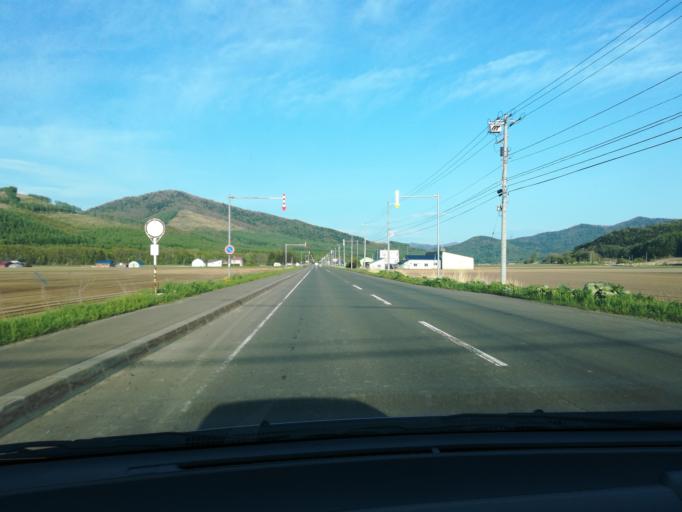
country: JP
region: Hokkaido
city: Shimo-furano
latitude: 43.1598
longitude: 142.5814
